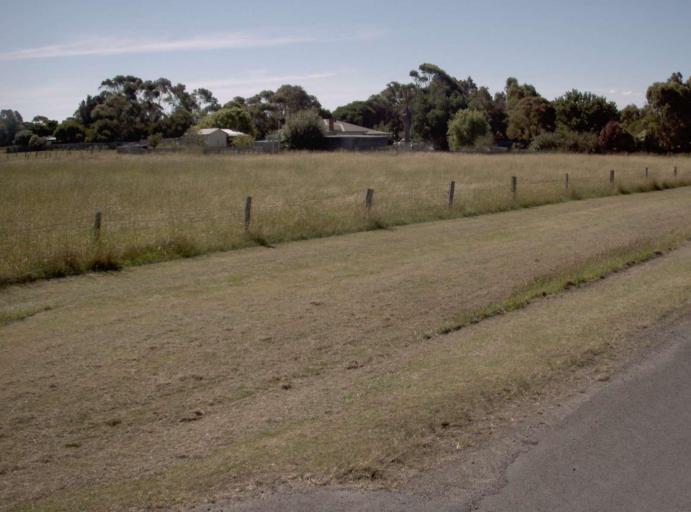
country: AU
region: Victoria
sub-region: Latrobe
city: Traralgon
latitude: -38.6193
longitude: 146.6682
